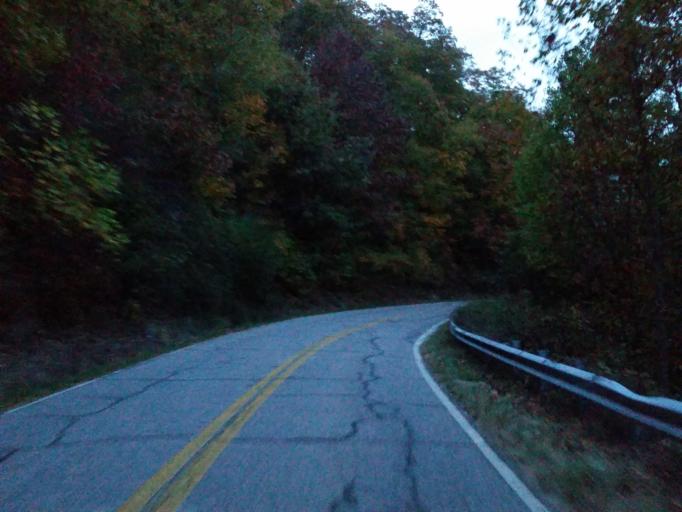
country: US
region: Georgia
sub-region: Lumpkin County
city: Dahlonega
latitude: 34.6583
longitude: -83.9739
